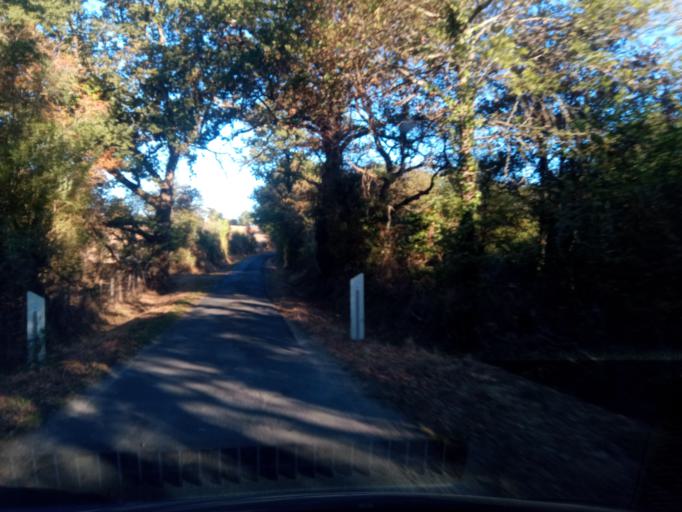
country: FR
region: Poitou-Charentes
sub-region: Departement de la Vienne
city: Montmorillon
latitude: 46.4115
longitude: 0.8676
